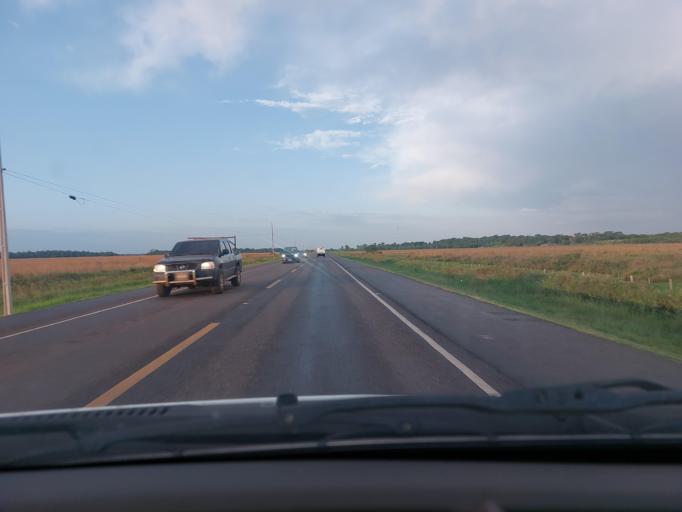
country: PY
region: San Pedro
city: Union
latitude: -24.8284
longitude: -56.7822
